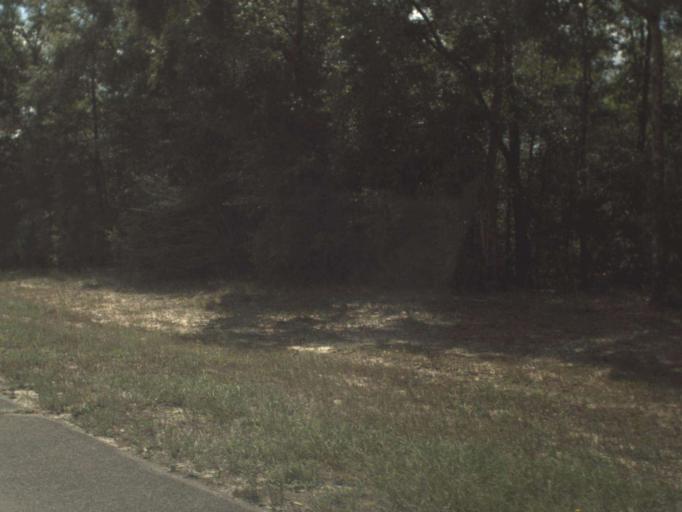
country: US
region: Florida
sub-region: Walton County
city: Freeport
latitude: 30.5674
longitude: -85.9221
